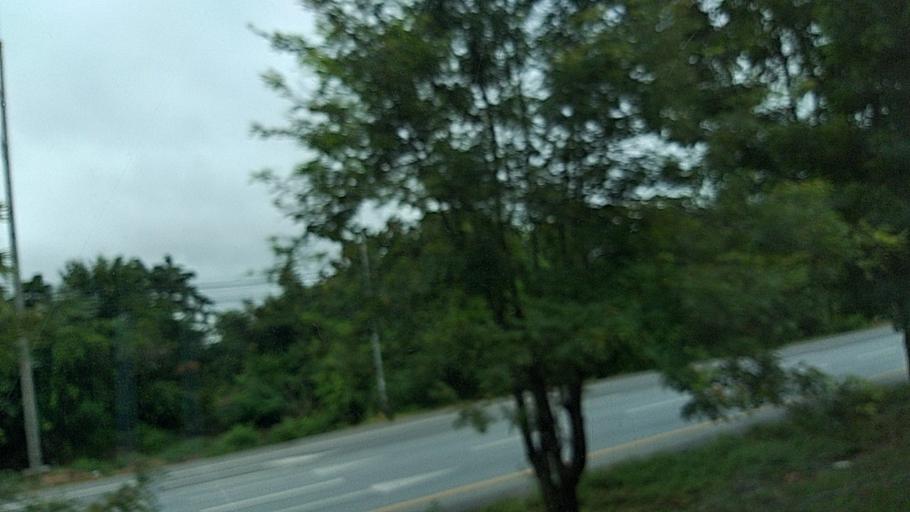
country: TH
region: Nakhon Ratchasima
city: Chaloem Phra Kiat
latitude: 15.0624
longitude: 102.1806
